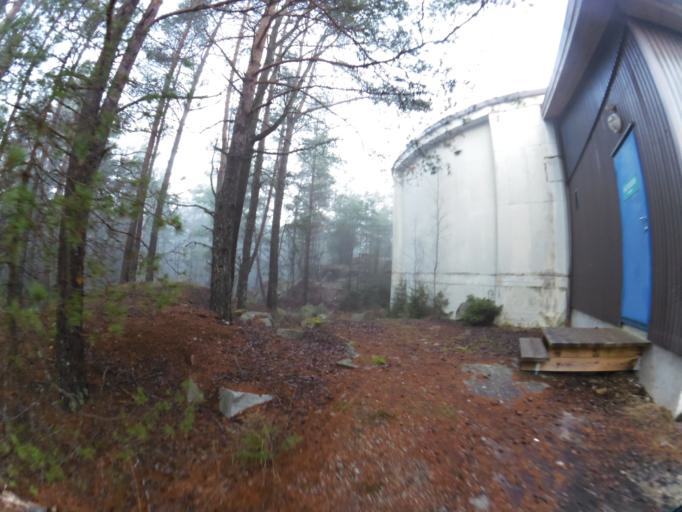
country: NO
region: Ostfold
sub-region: Fredrikstad
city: Fredrikstad
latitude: 59.2666
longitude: 10.9756
